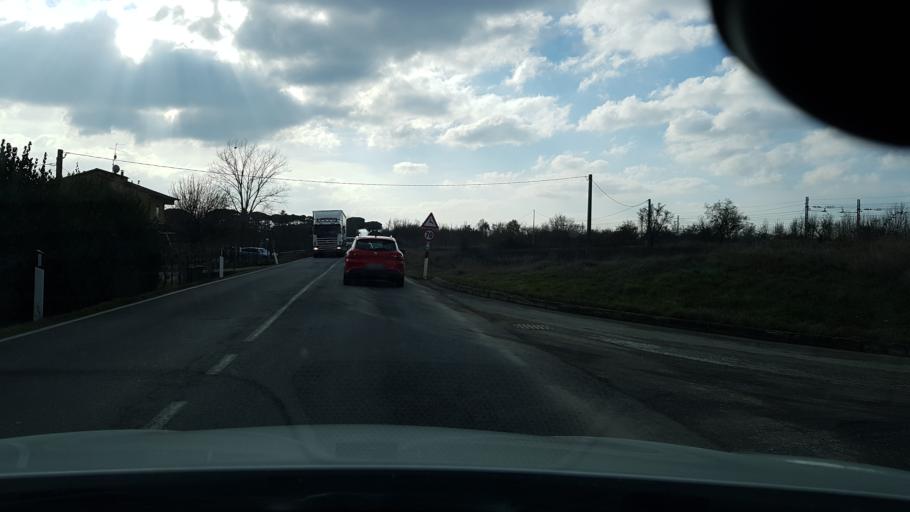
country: IT
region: Tuscany
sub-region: Province of Arezzo
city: Terontola
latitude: 43.1652
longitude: 12.0151
